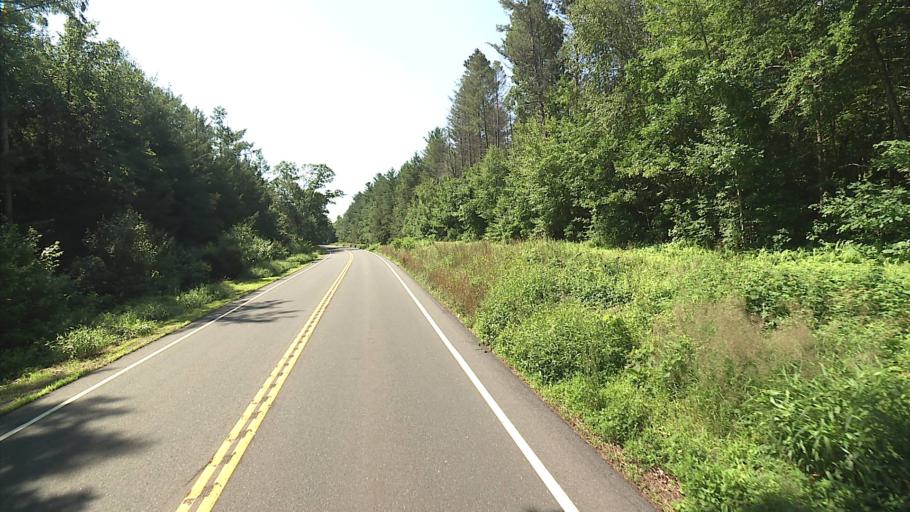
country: US
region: Connecticut
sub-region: Litchfield County
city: Terryville
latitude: 41.7105
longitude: -73.0118
